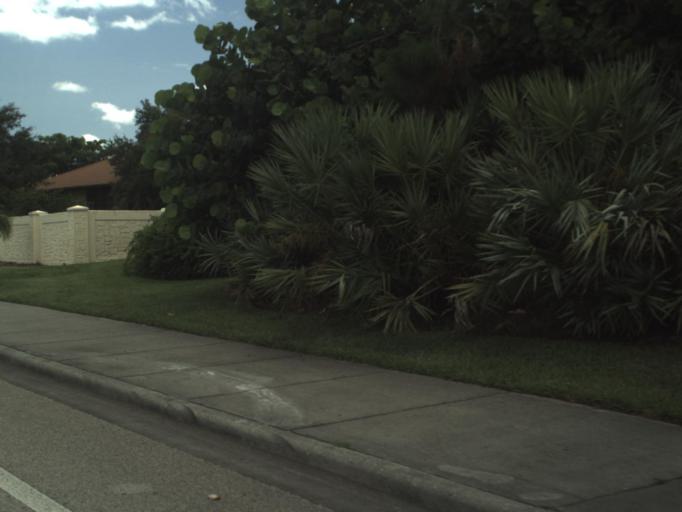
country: US
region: Florida
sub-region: Martin County
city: Palm City
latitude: 27.1539
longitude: -80.2452
